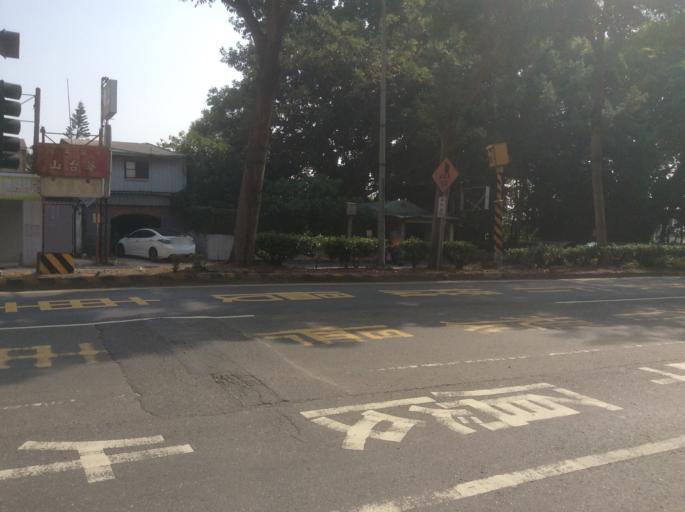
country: TW
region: Taiwan
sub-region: Tainan
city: Tainan
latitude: 22.9946
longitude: 120.2344
